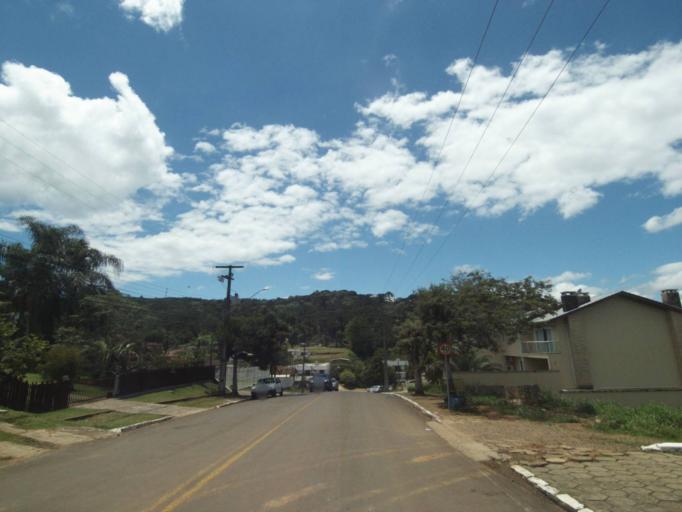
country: BR
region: Parana
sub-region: Pinhao
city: Pinhao
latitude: -26.1582
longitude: -51.5560
